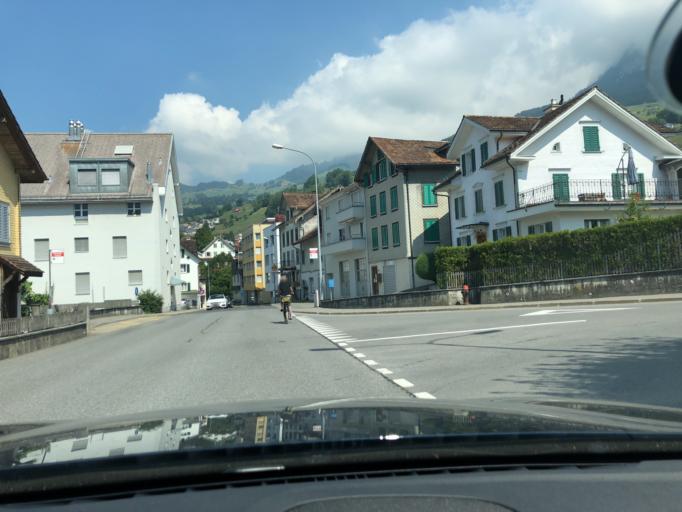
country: CH
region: Schwyz
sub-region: Bezirk Schwyz
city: Schwyz
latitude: 47.0187
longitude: 8.6579
